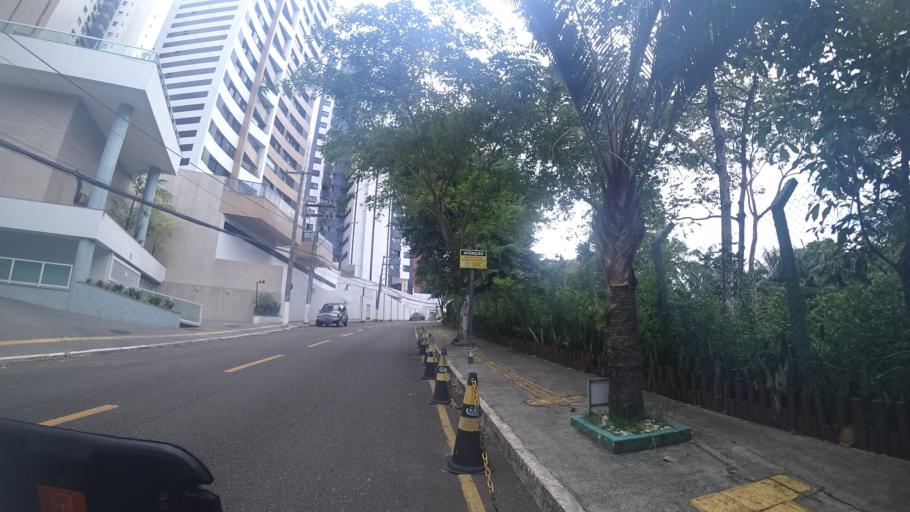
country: BR
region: Bahia
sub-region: Salvador
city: Salvador
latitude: -12.9995
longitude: -38.4681
